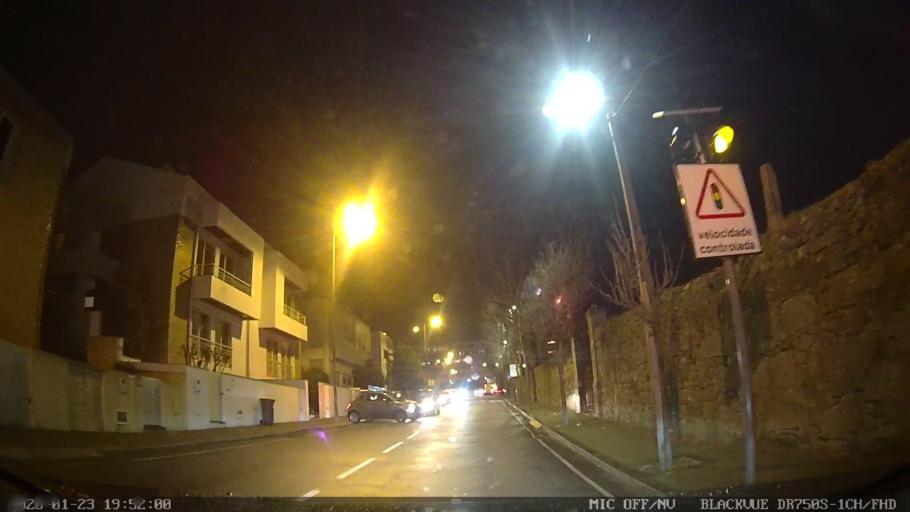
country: PT
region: Porto
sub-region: Maia
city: Maia
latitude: 41.2369
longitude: -8.6477
